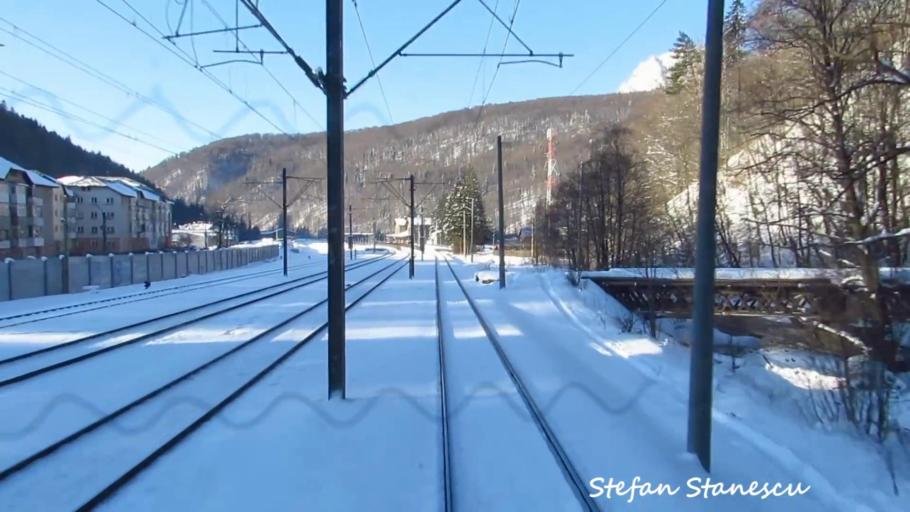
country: RO
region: Prahova
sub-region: Oras Azuga
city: Azuga
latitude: 45.4472
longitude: 25.5545
